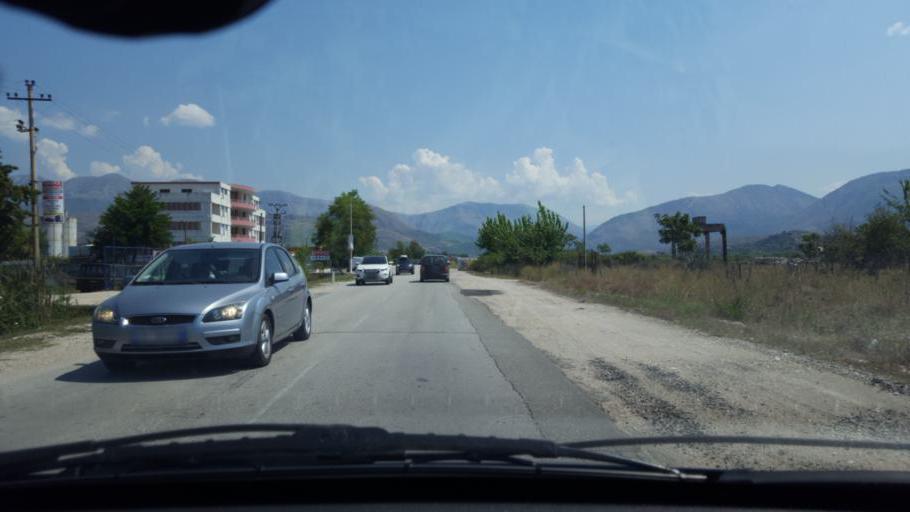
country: AL
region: Vlore
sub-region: Rrethi i Delvines
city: Finiq
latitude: 39.8895
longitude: 20.0623
